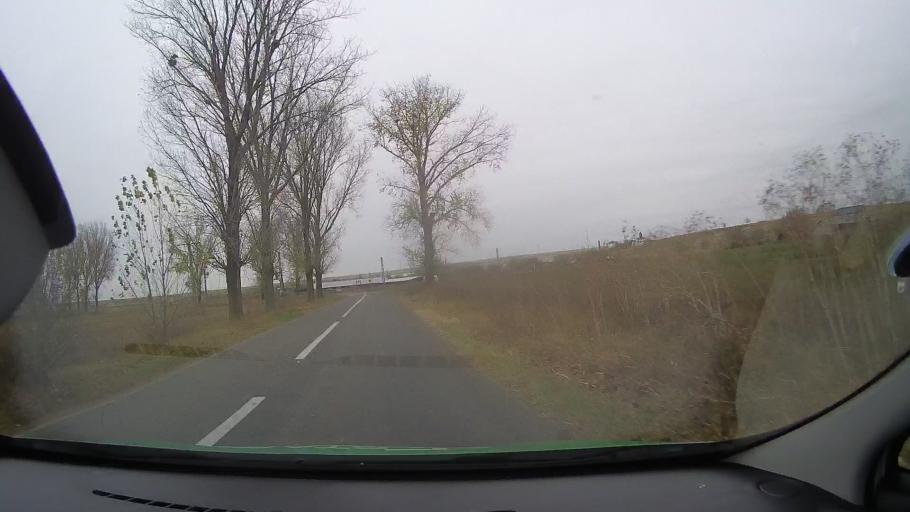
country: RO
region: Constanta
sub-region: Comuna Saraiu
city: Saraiu
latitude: 44.7255
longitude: 28.2206
